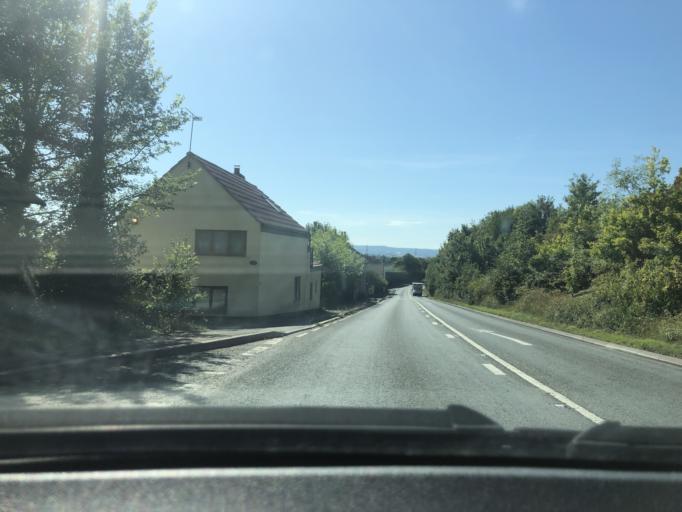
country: GB
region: England
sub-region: Somerset
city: Woolavington
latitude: 51.1549
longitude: -2.9463
